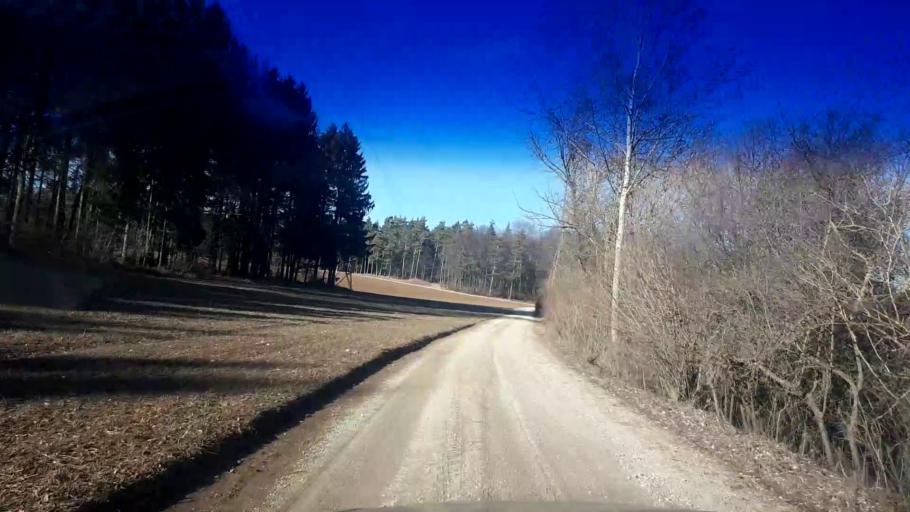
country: DE
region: Bavaria
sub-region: Upper Franconia
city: Poxdorf
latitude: 49.9649
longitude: 11.0857
